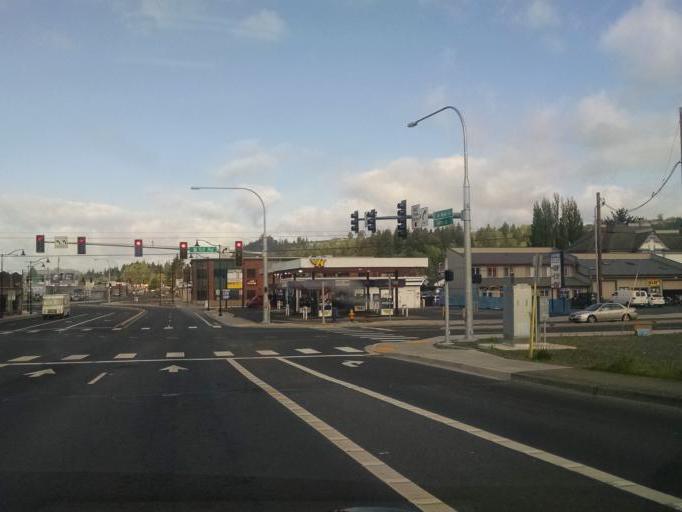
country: US
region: Washington
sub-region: Cowlitz County
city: Kelso
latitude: 46.1455
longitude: -122.9157
